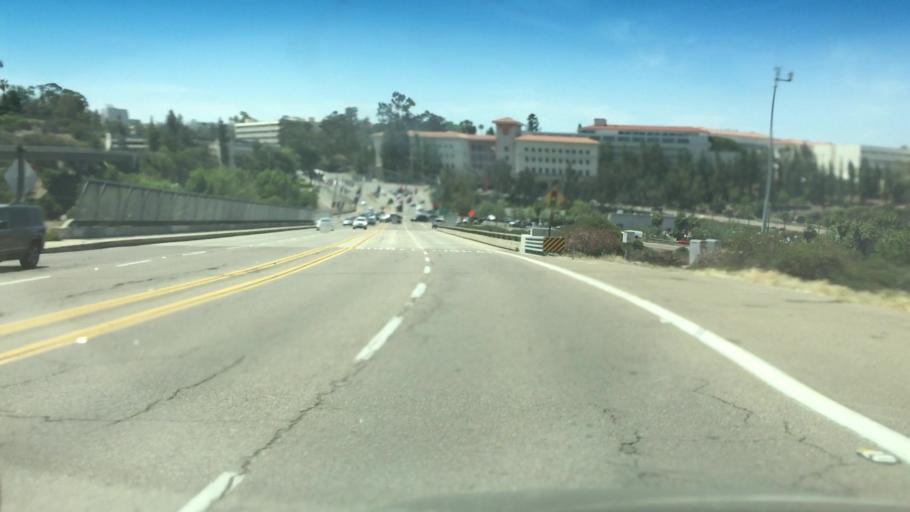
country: US
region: California
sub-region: San Diego County
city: La Mesa
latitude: 32.7802
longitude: -117.0659
